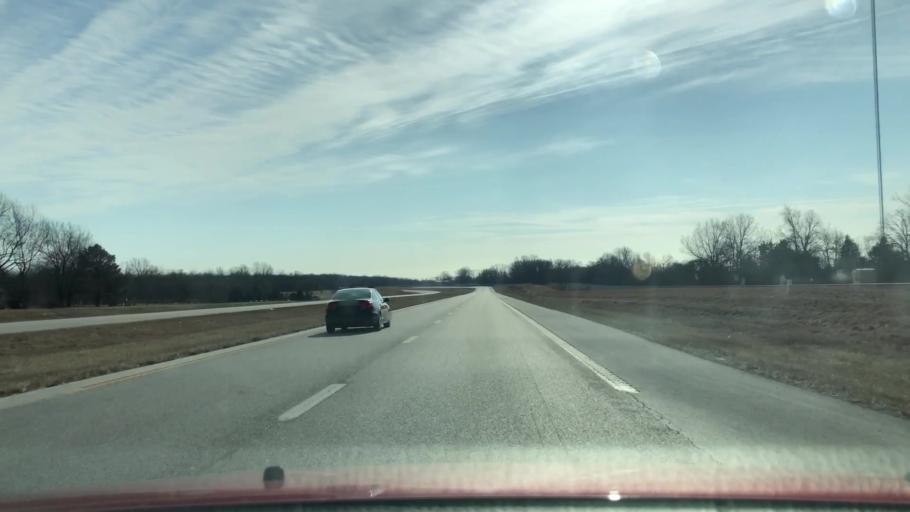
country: US
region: Missouri
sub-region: Webster County
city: Seymour
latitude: 37.1383
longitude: -92.7447
